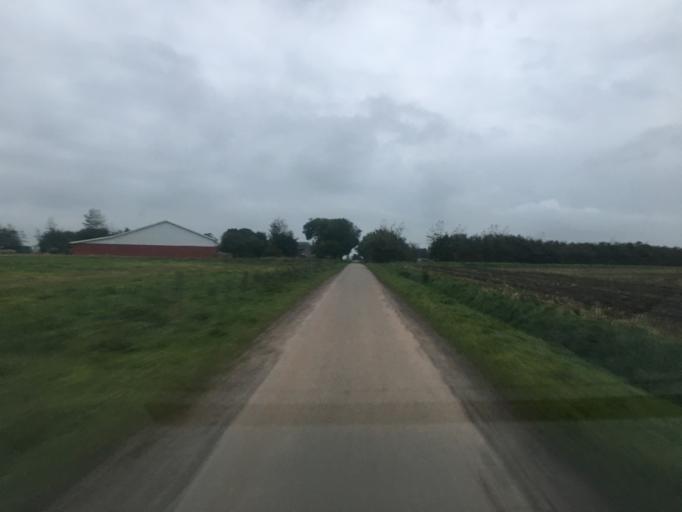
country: DK
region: South Denmark
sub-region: Tonder Kommune
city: Sherrebek
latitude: 55.0443
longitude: 8.8093
